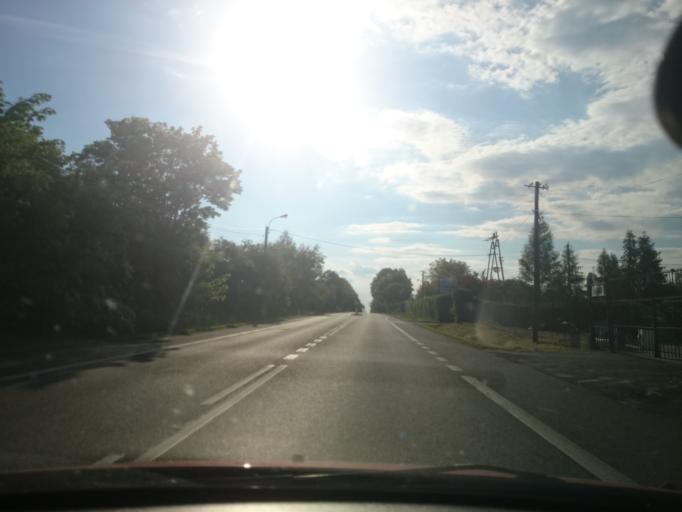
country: PL
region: Opole Voivodeship
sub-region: Powiat strzelecki
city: Jemielnica
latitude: 50.4897
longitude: 18.4055
